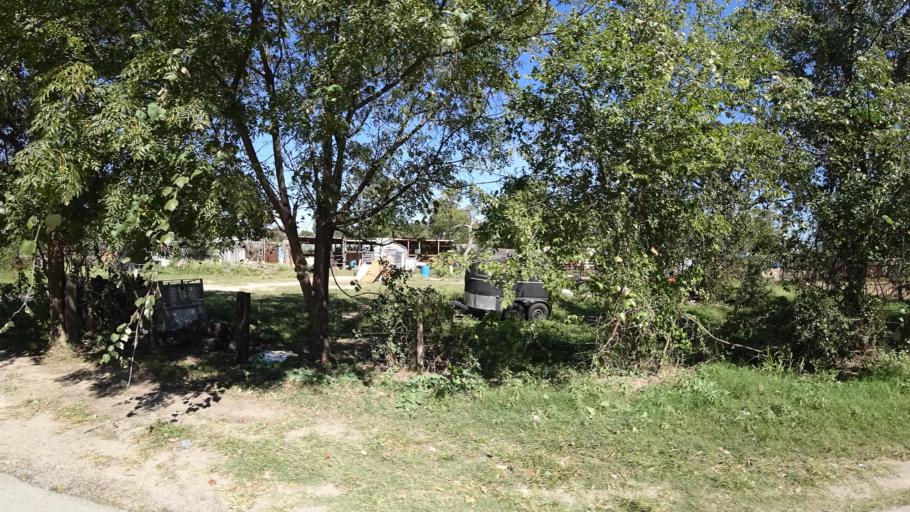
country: US
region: Texas
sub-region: Travis County
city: Austin
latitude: 30.2700
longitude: -97.6718
